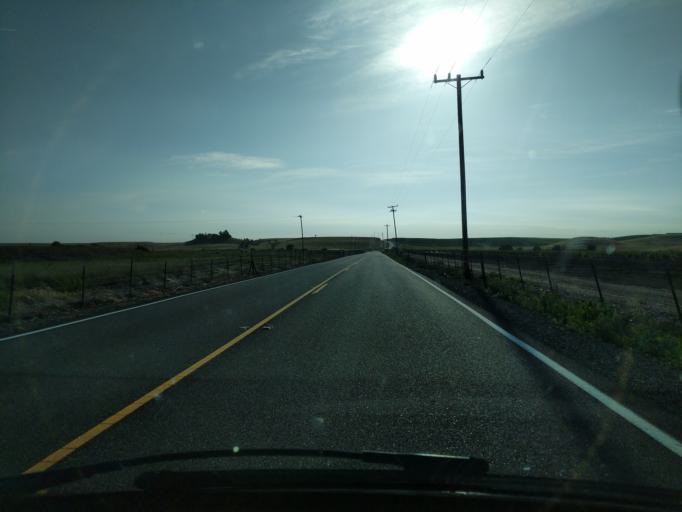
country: US
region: California
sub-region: Stanislaus County
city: East Oakdale
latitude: 37.9449
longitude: -120.8881
